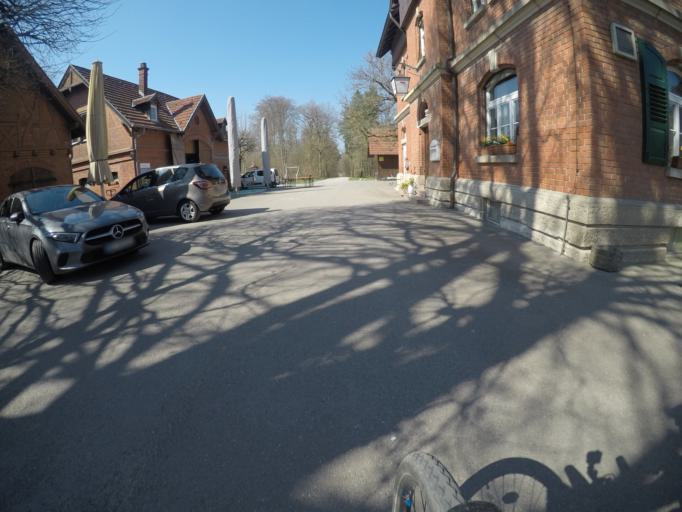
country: DE
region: Baden-Wuerttemberg
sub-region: Regierungsbezirk Stuttgart
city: Gerlingen
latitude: 48.7449
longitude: 9.0618
